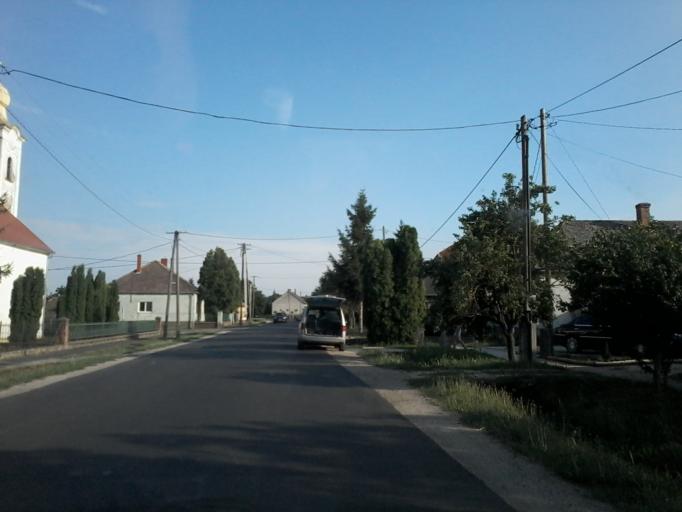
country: HU
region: Vas
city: Sarvar
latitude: 47.2168
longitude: 17.0160
